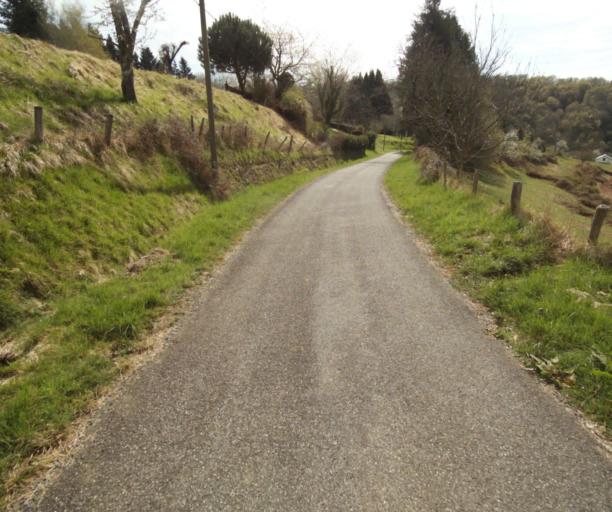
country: FR
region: Limousin
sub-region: Departement de la Correze
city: Laguenne
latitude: 45.2525
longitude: 1.8195
